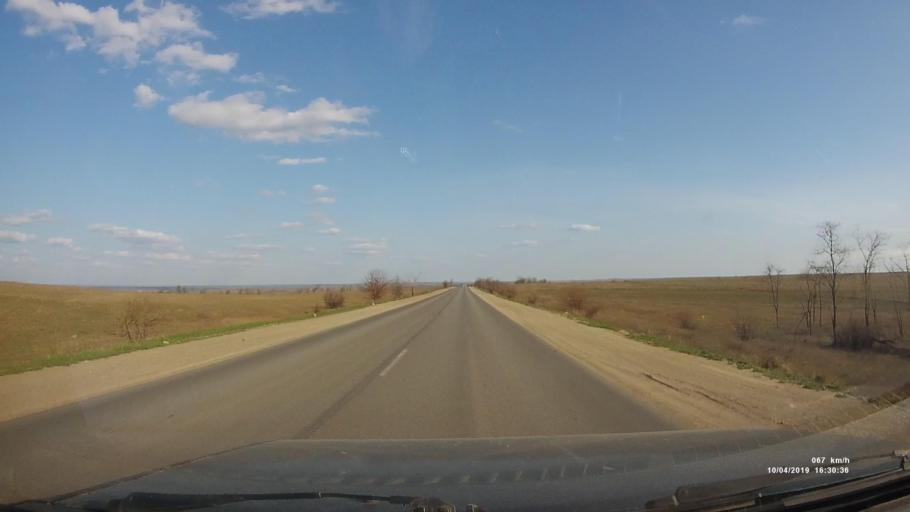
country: RU
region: Rostov
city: Staraya Stanitsa
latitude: 48.2609
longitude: 40.3669
